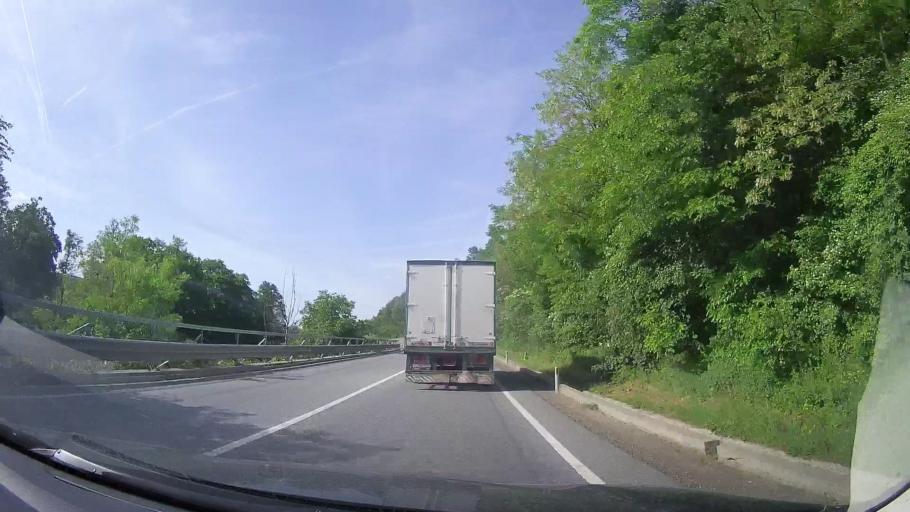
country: RO
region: Caras-Severin
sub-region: Comuna Slatina-Timis
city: Slatina-Timis
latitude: 45.2388
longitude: 22.3017
